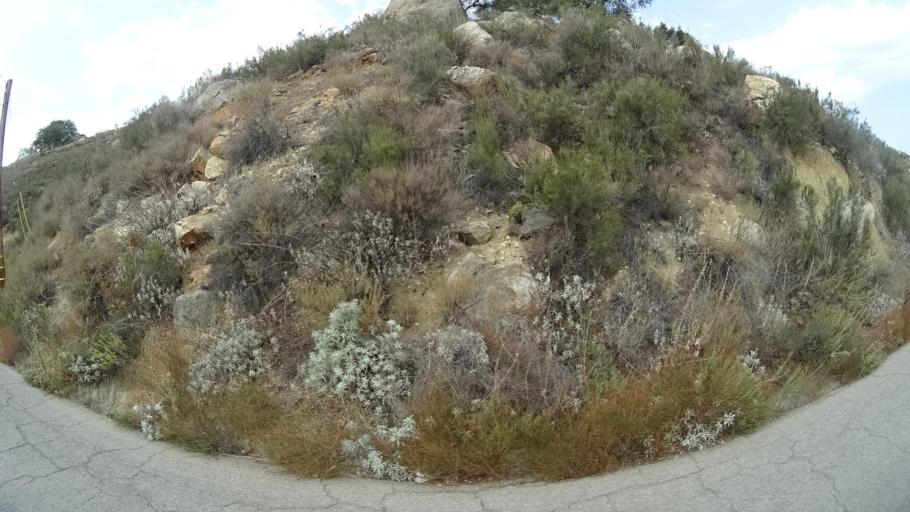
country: US
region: California
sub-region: San Diego County
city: San Diego Country Estates
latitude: 33.1005
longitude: -116.7891
